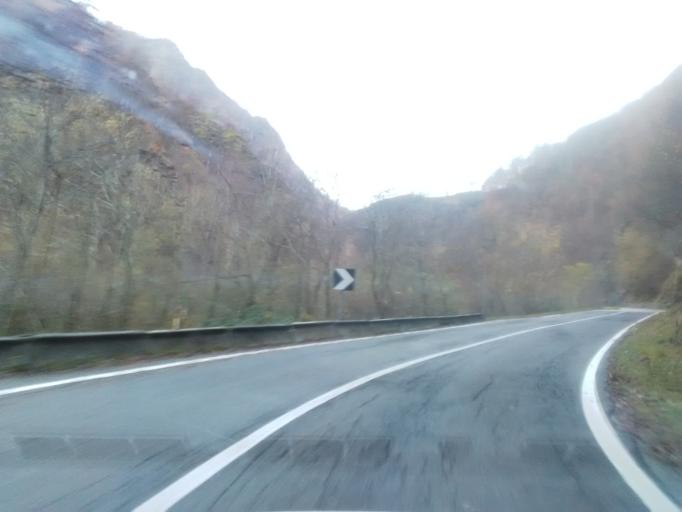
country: IT
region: Piedmont
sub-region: Provincia di Vercelli
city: Cervatto
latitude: 45.8736
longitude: 8.1822
